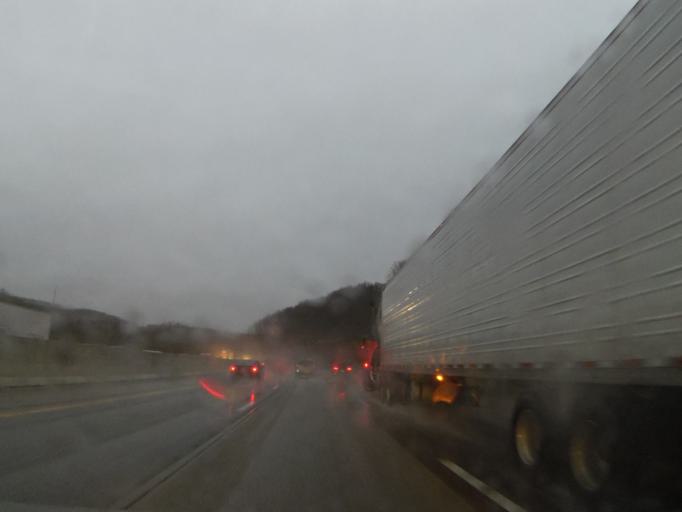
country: US
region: Kentucky
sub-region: Rockcastle County
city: Mount Vernon
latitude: 37.2466
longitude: -84.2458
